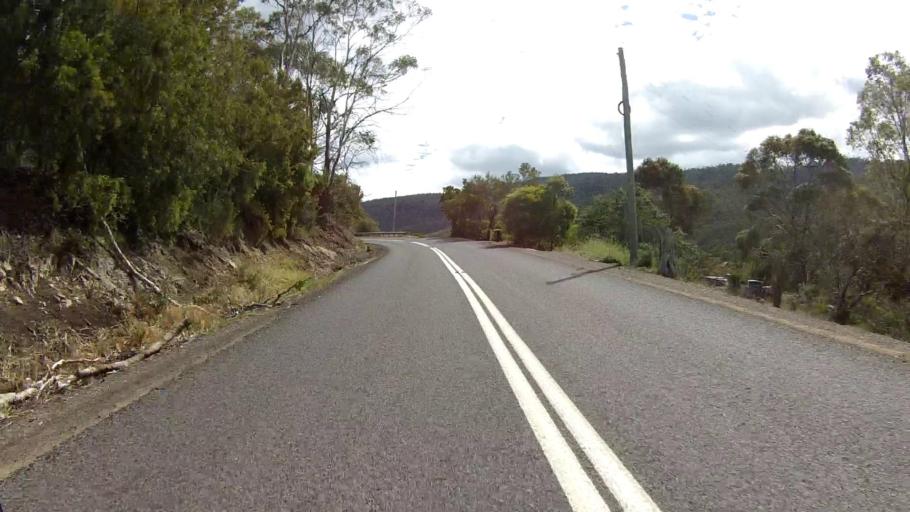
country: AU
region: Tasmania
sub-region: Clarence
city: Lindisfarne
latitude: -42.8048
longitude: 147.3548
